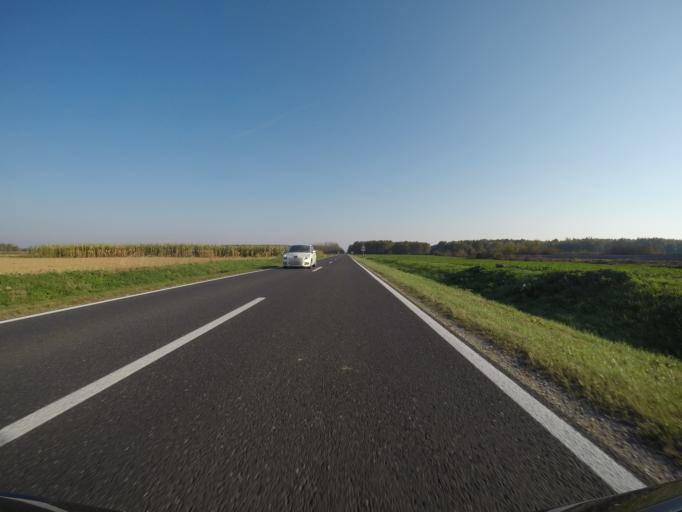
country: HR
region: Koprivnicko-Krizevacka
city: Kalinovac
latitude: 46.0018
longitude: 17.1138
